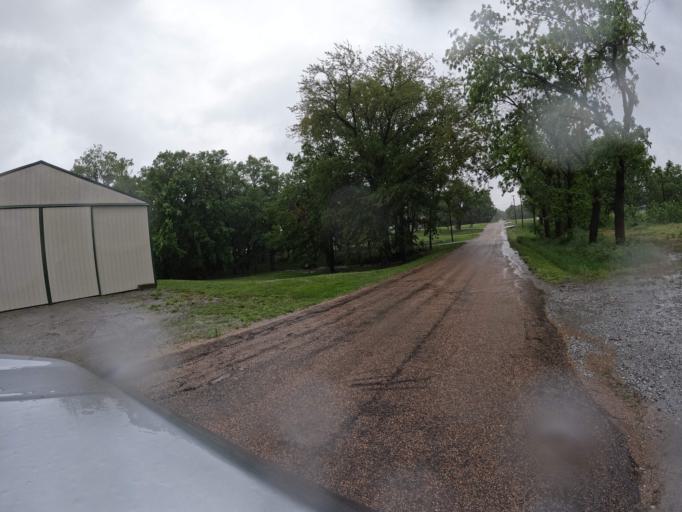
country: US
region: Nebraska
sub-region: Gage County
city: Wymore
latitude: 40.1182
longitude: -96.6697
